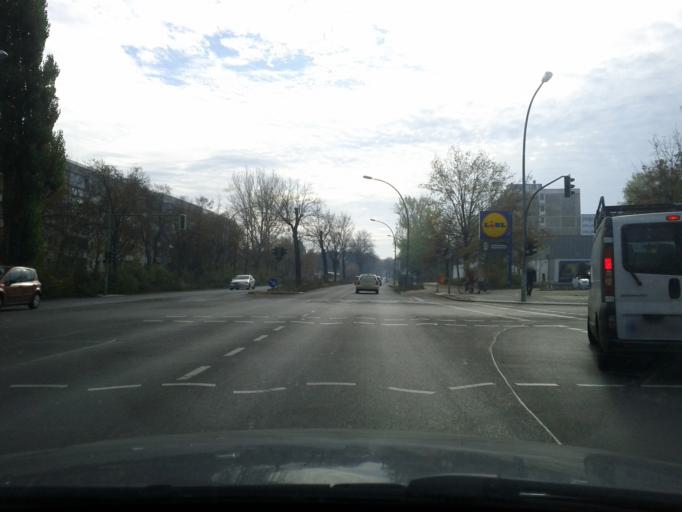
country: DE
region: Berlin
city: Berlin Koepenick
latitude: 52.4476
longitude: 13.5937
